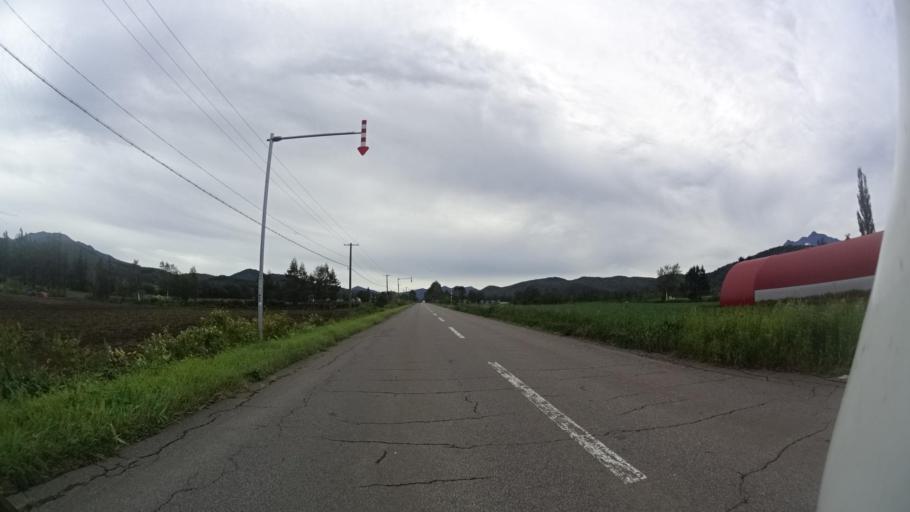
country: JP
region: Hokkaido
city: Shibetsu
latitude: 43.8664
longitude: 144.7530
